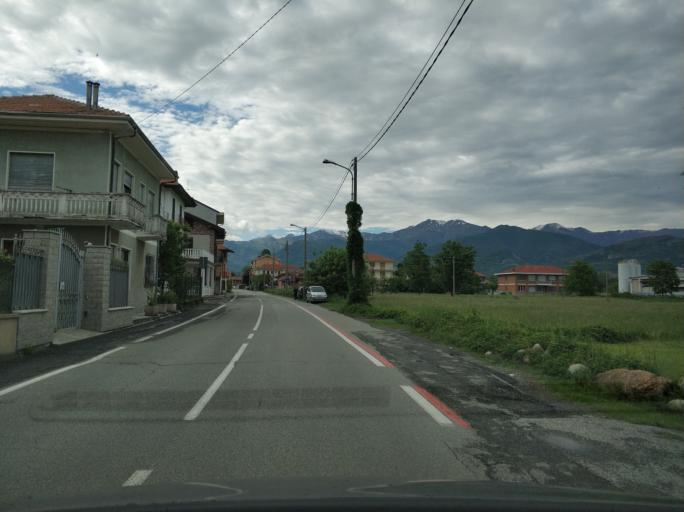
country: IT
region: Piedmont
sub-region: Provincia di Torino
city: Cafasse
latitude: 45.2511
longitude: 7.5136
